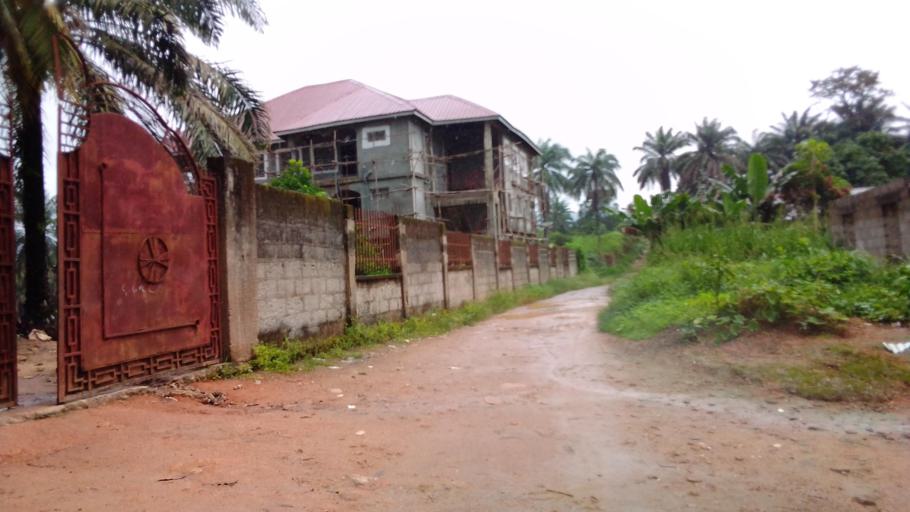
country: SL
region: Eastern Province
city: Kenema
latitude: 7.8763
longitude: -11.1705
